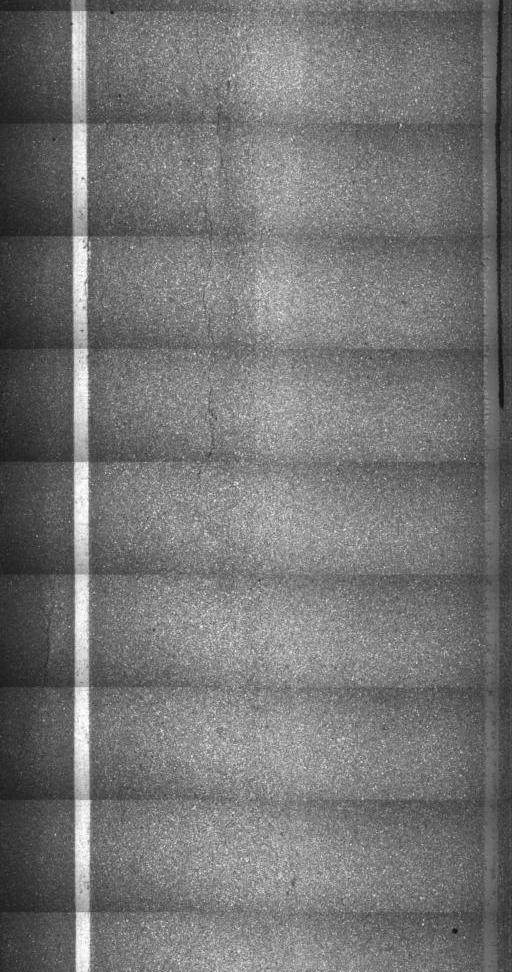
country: US
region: Vermont
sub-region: Orange County
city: Randolph
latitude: 43.9663
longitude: -72.8425
